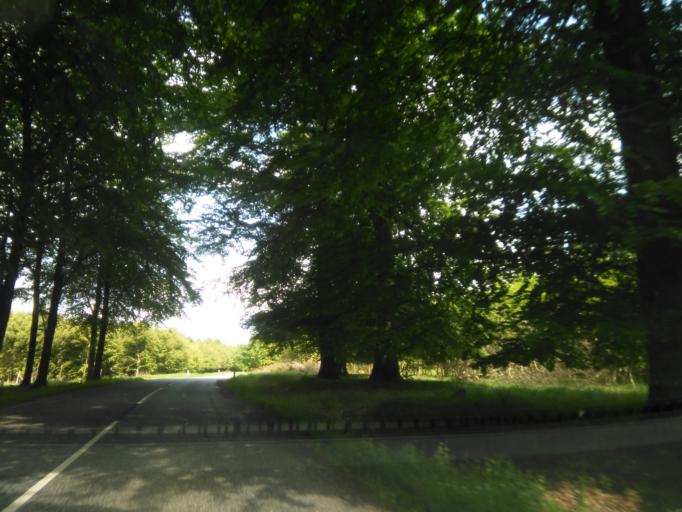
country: DK
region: Central Jutland
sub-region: Favrskov Kommune
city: Hammel
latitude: 56.2425
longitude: 9.9297
